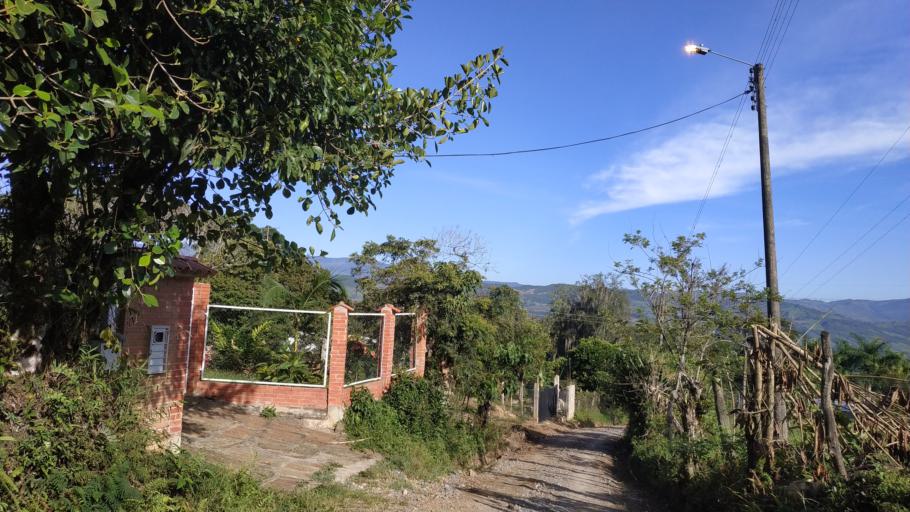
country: CO
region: Santander
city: Guepsa
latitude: 6.0248
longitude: -73.5266
